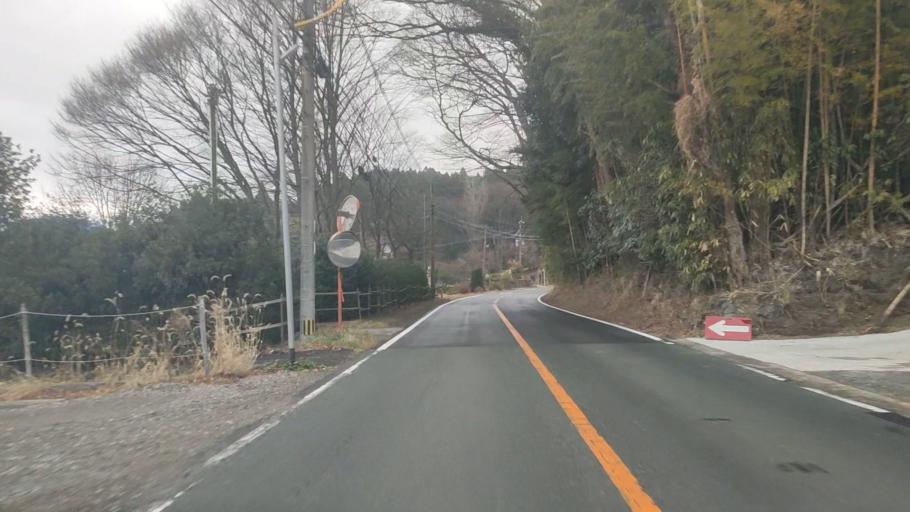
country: JP
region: Kumamoto
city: Aso
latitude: 32.8570
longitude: 131.1595
